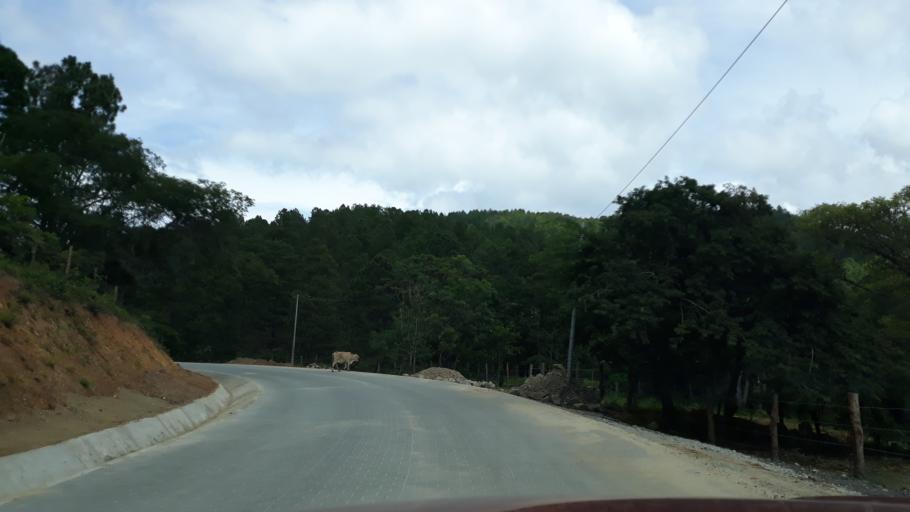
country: HN
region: El Paraiso
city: Santa Cruz
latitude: 13.7446
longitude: -86.6261
